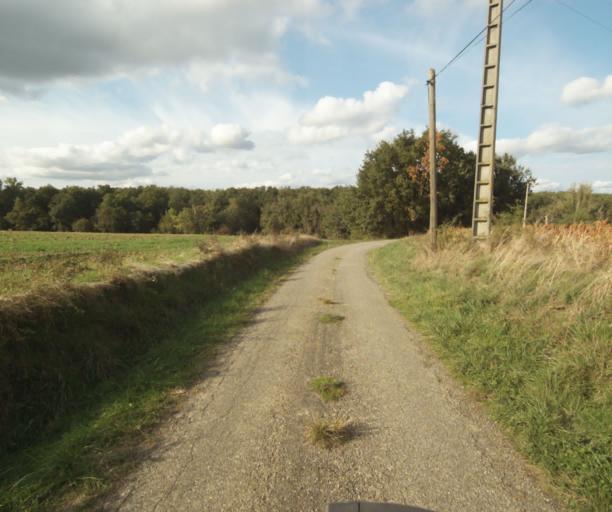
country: FR
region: Midi-Pyrenees
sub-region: Departement du Tarn-et-Garonne
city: Verdun-sur-Garonne
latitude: 43.8432
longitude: 1.1460
